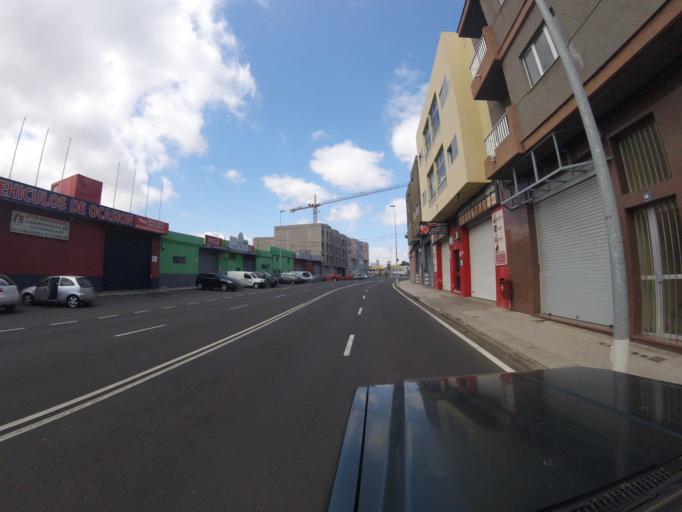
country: ES
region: Canary Islands
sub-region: Provincia de Santa Cruz de Tenerife
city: La Laguna
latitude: 28.4242
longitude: -16.3179
